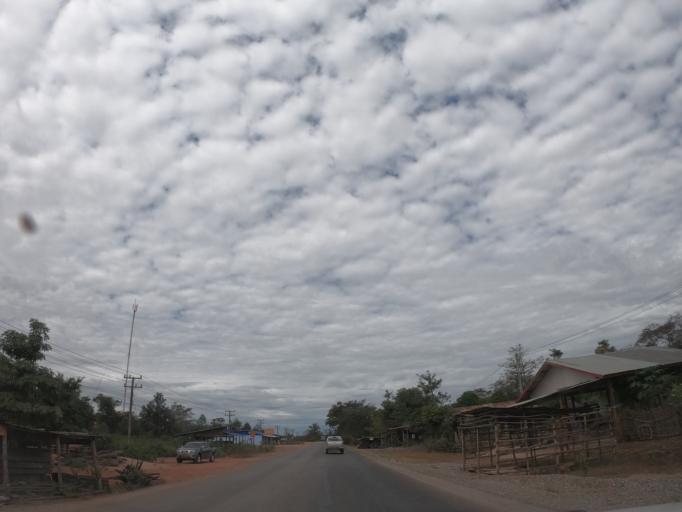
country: TH
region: Nakhon Phanom
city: Nakhon Phanom
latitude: 17.5240
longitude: 104.7253
